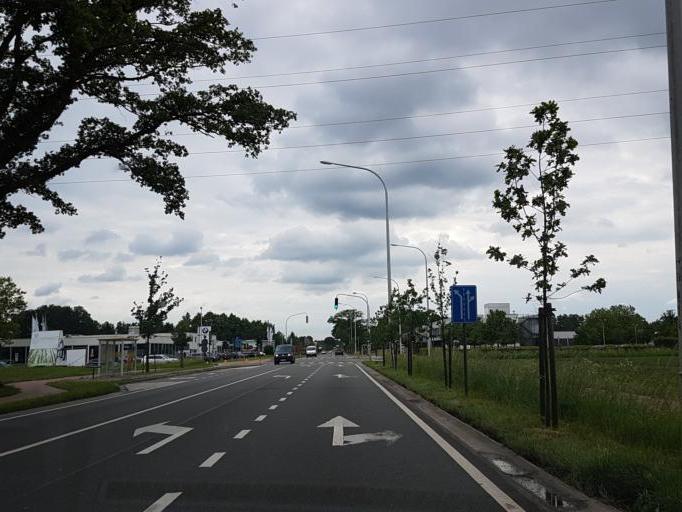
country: BE
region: Flanders
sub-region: Provincie Antwerpen
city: Oostmalle
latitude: 51.2990
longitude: 4.7131
